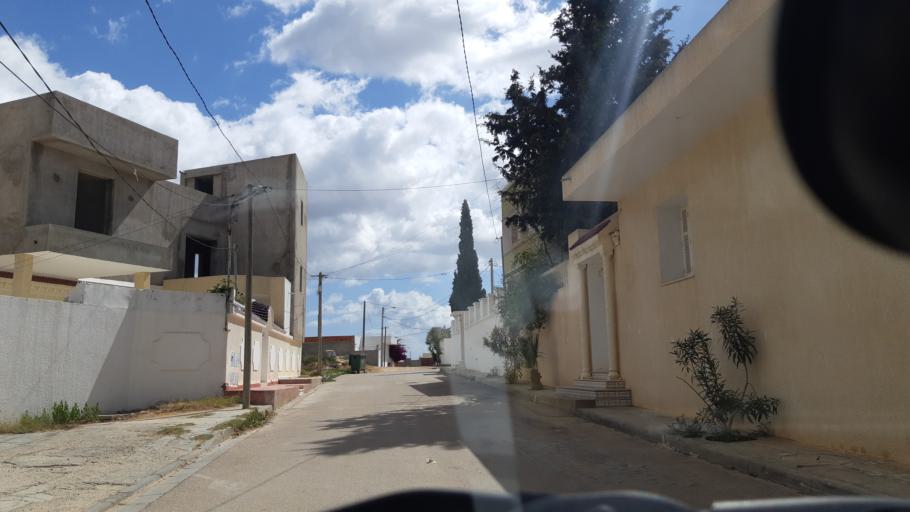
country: TN
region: Susah
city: Akouda
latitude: 35.8782
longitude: 10.5451
